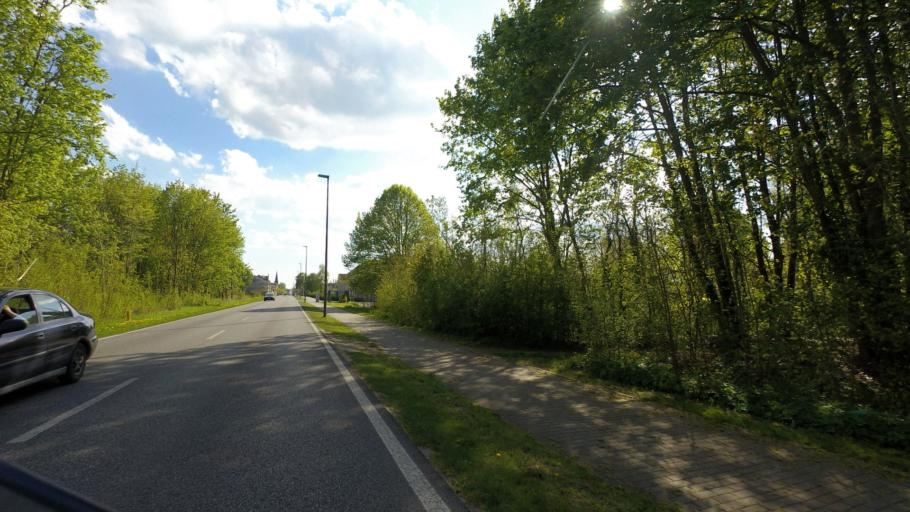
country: DE
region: Brandenburg
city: Zehdenick
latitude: 52.9969
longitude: 13.3467
